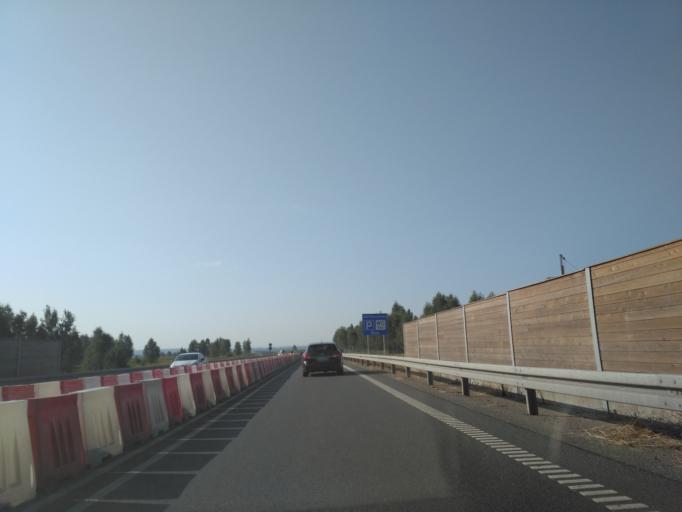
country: PL
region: Subcarpathian Voivodeship
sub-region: Powiat rzeszowski
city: Sokolow Malopolski
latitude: 50.2453
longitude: 22.1373
